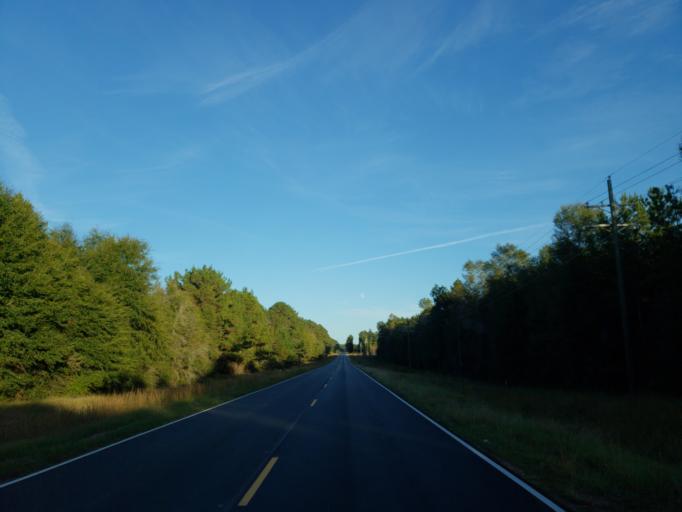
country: US
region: Mississippi
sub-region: Wayne County
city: Belmont
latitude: 31.4214
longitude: -88.5300
